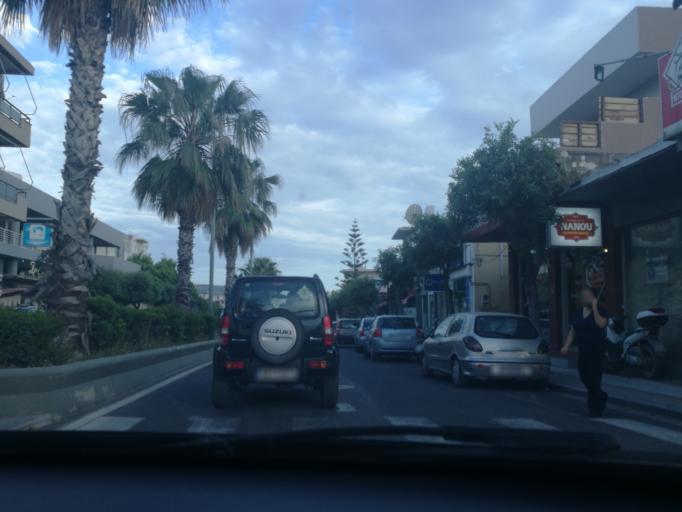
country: GR
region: Crete
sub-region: Nomos Irakleiou
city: Irakleion
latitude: 35.3164
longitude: 25.1463
